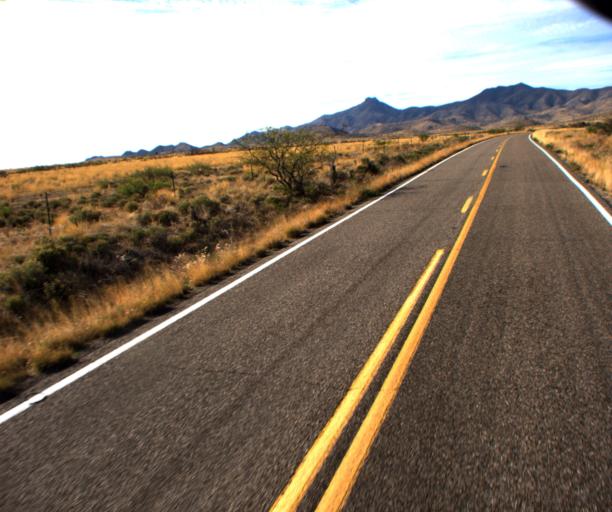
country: US
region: Arizona
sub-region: Cochise County
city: Willcox
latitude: 32.1214
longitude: -109.5554
